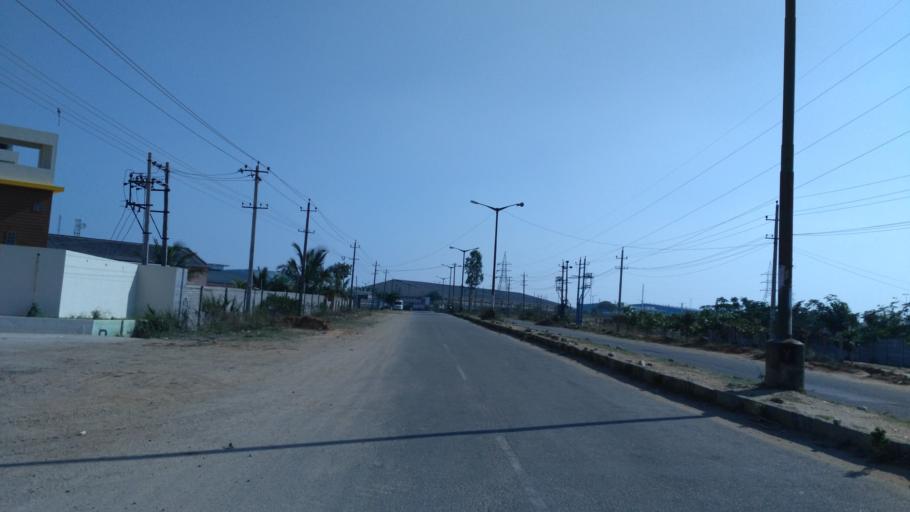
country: IN
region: Karnataka
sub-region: Hassan
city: Hassan
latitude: 12.9785
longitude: 76.1207
